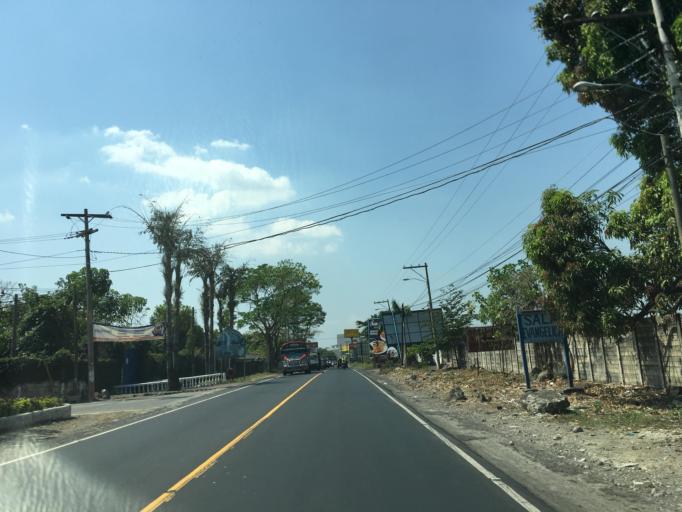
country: GT
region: Escuintla
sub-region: Municipio de Escuintla
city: Escuintla
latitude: 14.2972
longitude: -90.7950
